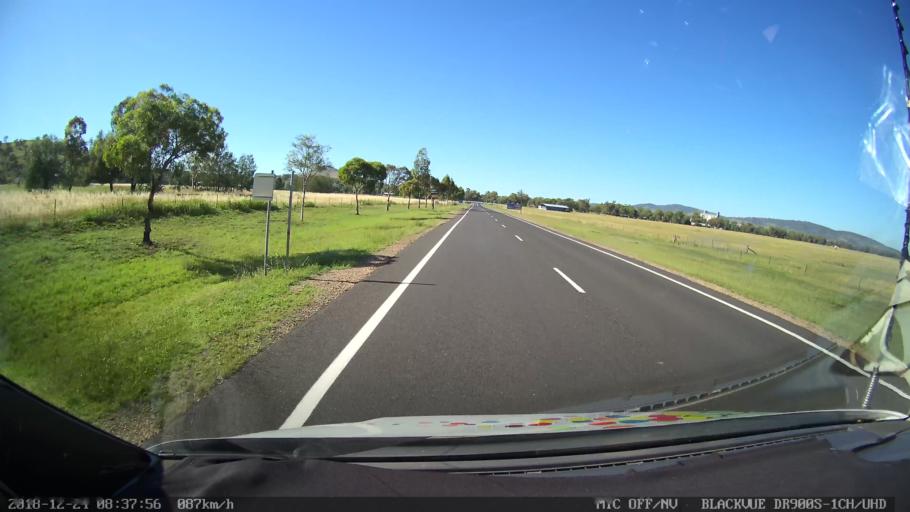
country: AU
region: New South Wales
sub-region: Liverpool Plains
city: Quirindi
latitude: -31.3357
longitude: 150.6479
